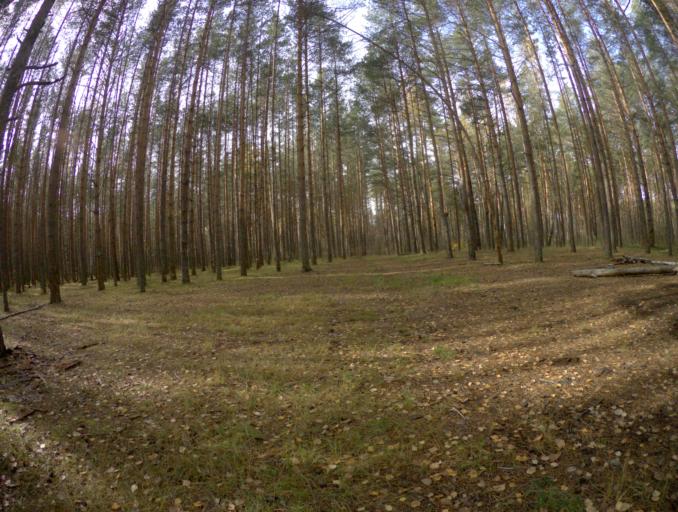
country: RU
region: Vladimir
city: Kommunar
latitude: 56.1187
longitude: 40.4689
